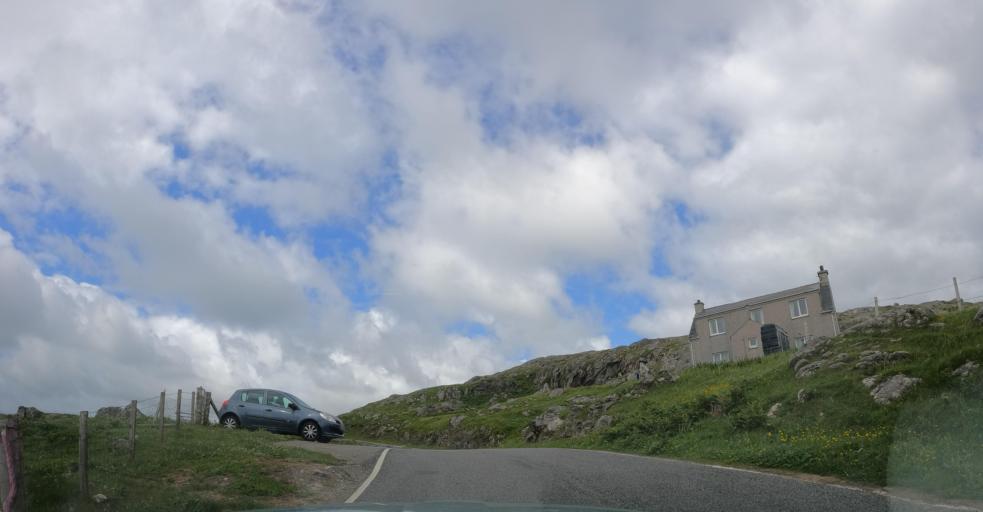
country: GB
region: Scotland
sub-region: Eilean Siar
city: Isle of South Uist
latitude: 57.0746
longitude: -7.3019
